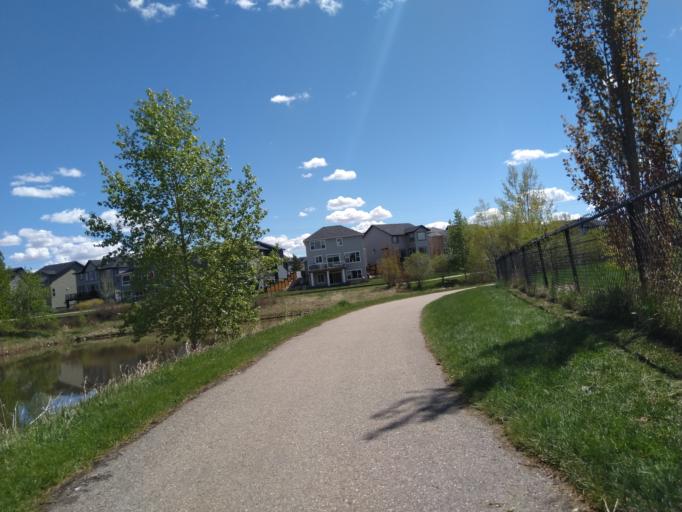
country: CA
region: Alberta
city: Chestermere
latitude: 51.0265
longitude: -113.8344
